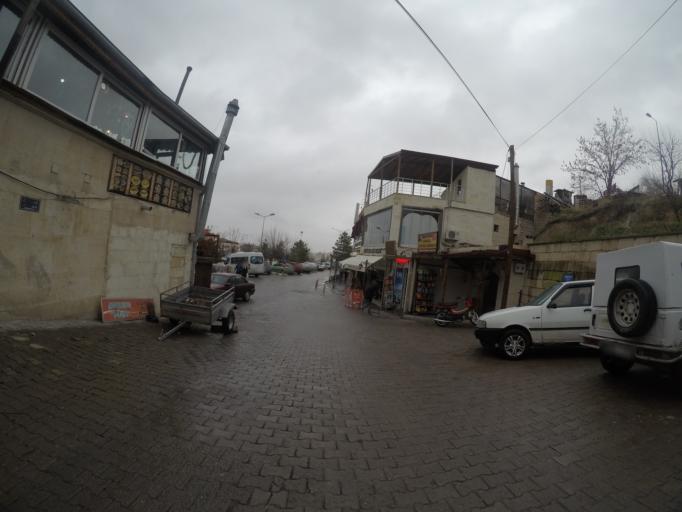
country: TR
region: Nevsehir
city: Goereme
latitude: 38.6436
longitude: 34.8318
